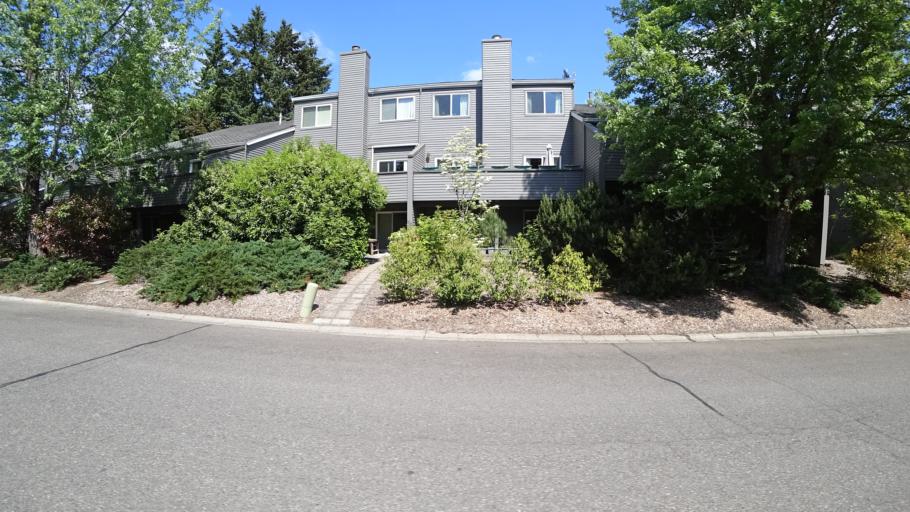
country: US
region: Oregon
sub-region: Clackamas County
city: Lake Oswego
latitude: 45.4325
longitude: -122.7068
